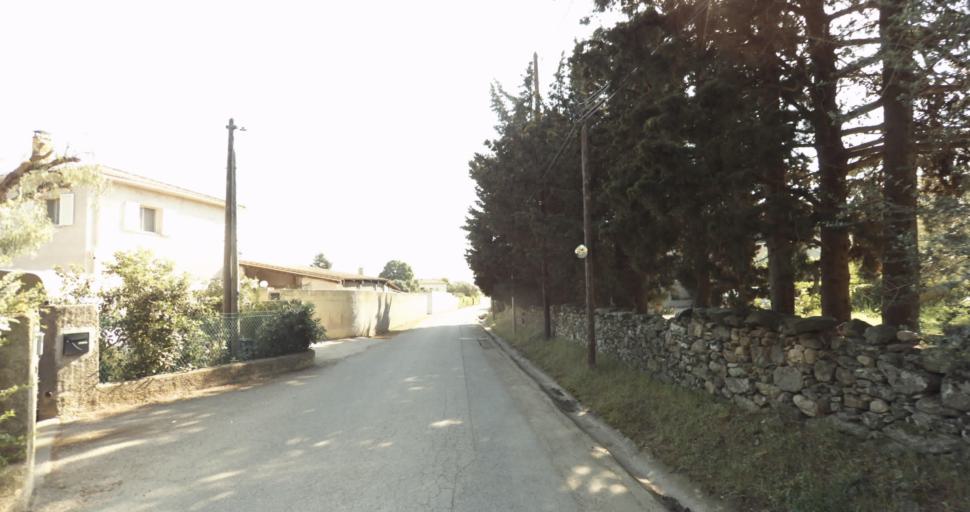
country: FR
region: Corsica
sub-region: Departement de la Haute-Corse
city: Biguglia
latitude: 42.6334
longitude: 9.4293
